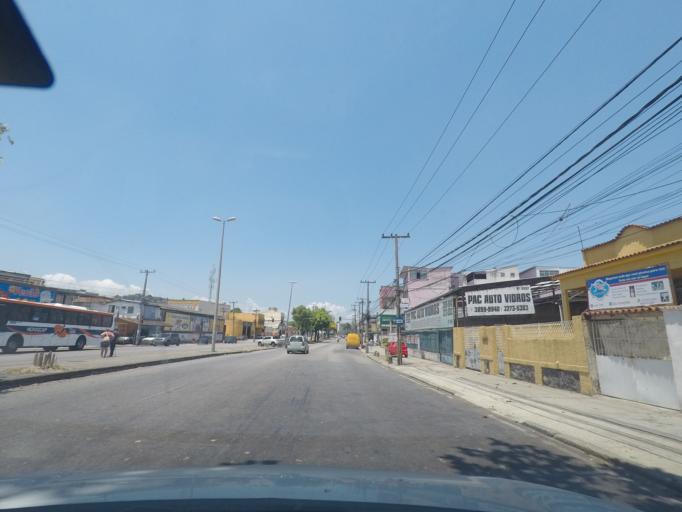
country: BR
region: Rio de Janeiro
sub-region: Rio De Janeiro
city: Rio de Janeiro
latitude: -22.8833
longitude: -43.2964
